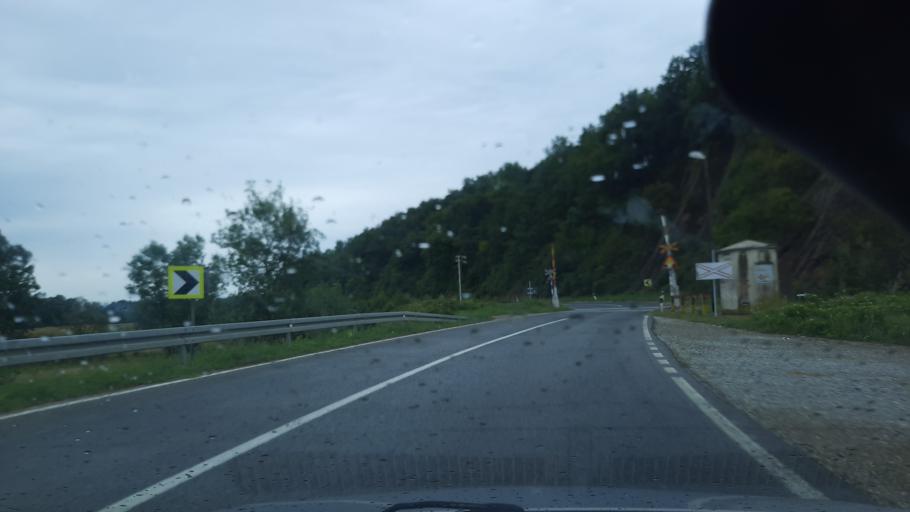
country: RS
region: Central Serbia
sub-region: Sumadijski Okrug
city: Knic
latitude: 43.8500
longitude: 20.7718
